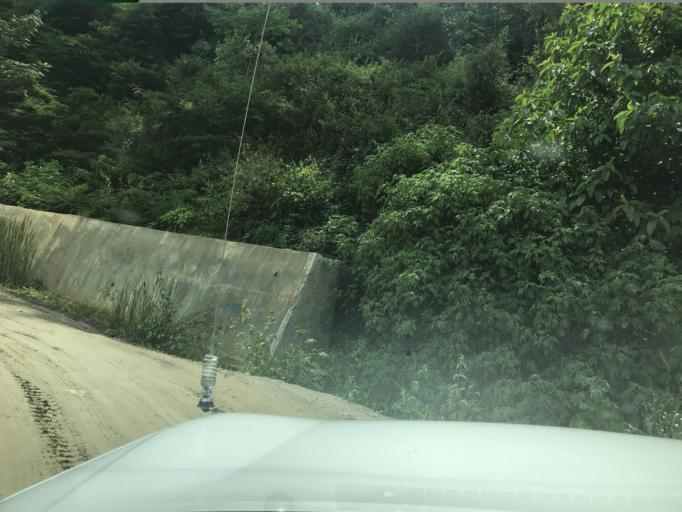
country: TL
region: Aileu
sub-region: Aileu Villa
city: Aileu
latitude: -8.6611
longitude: 125.5490
